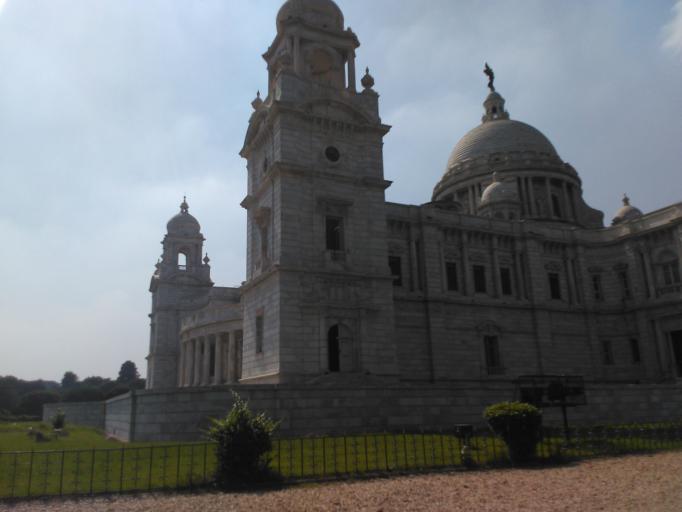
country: IN
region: West Bengal
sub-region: Kolkata
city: Bara Bazar
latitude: 22.5454
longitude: 88.3433
